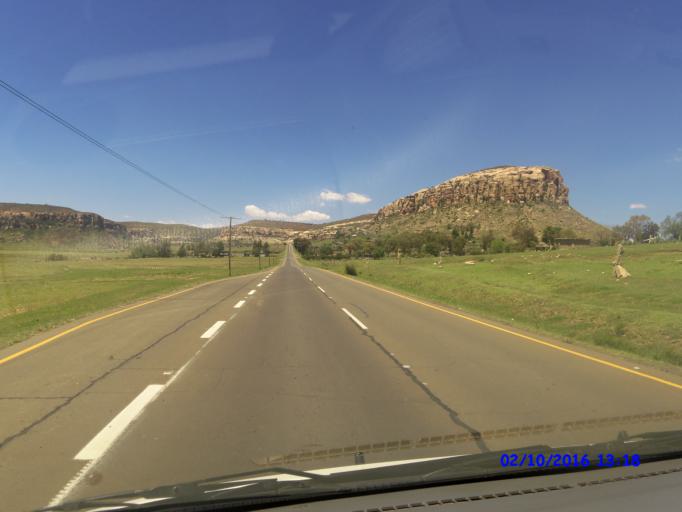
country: LS
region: Maseru
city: Nako
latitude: -29.4236
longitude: 27.6798
